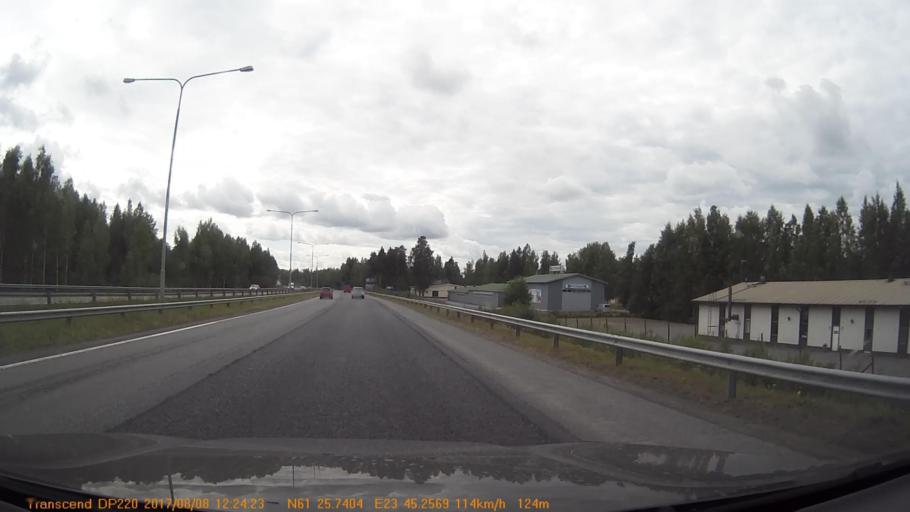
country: FI
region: Pirkanmaa
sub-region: Tampere
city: Tampere
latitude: 61.4289
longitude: 23.7542
